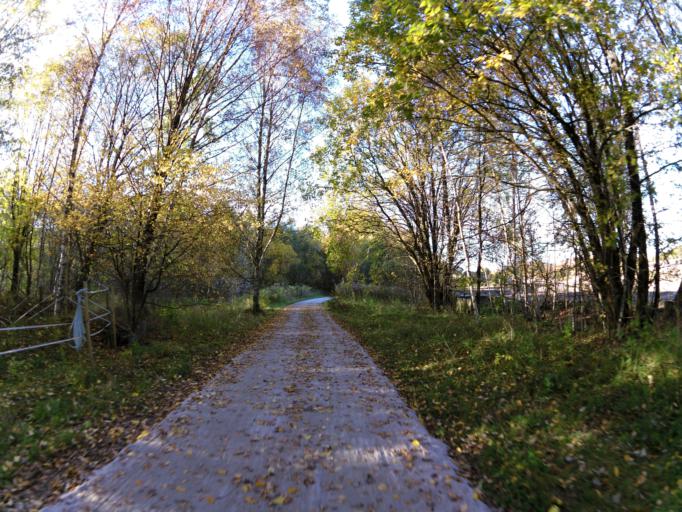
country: NO
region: Ostfold
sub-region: Sarpsborg
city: Sarpsborg
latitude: 59.2668
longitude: 11.0989
